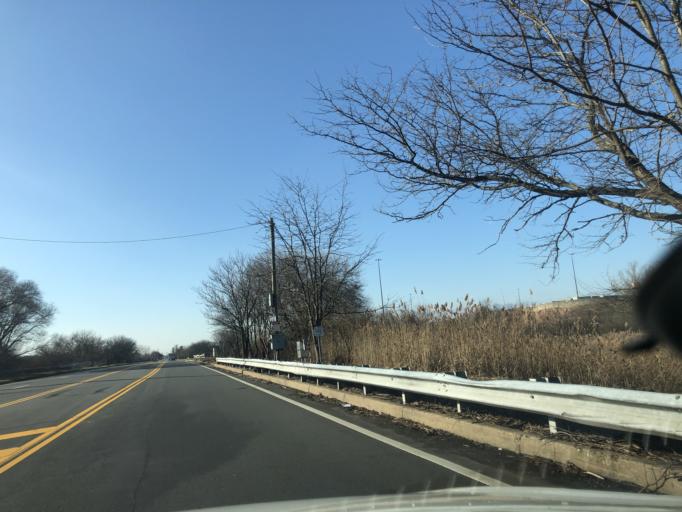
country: US
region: New Jersey
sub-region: Gloucester County
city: National Park
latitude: 39.8865
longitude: -75.2177
